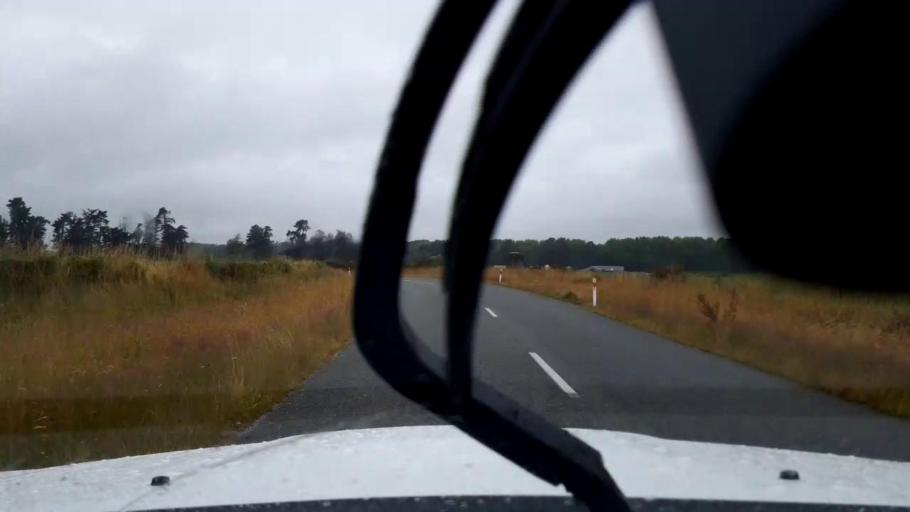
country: NZ
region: Canterbury
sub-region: Timaru District
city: Pleasant Point
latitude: -44.2538
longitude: 171.2390
